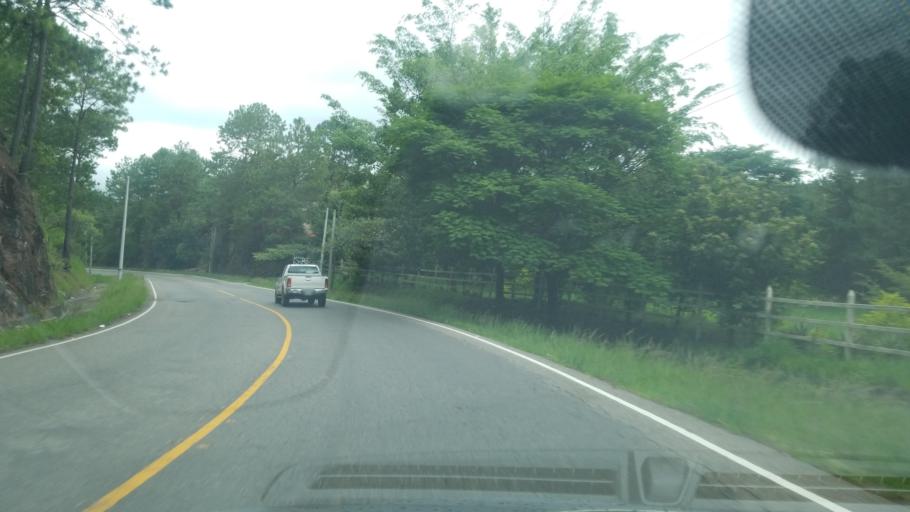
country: HN
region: Ocotepeque
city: Sinuapa
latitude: 14.4634
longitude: -89.1591
